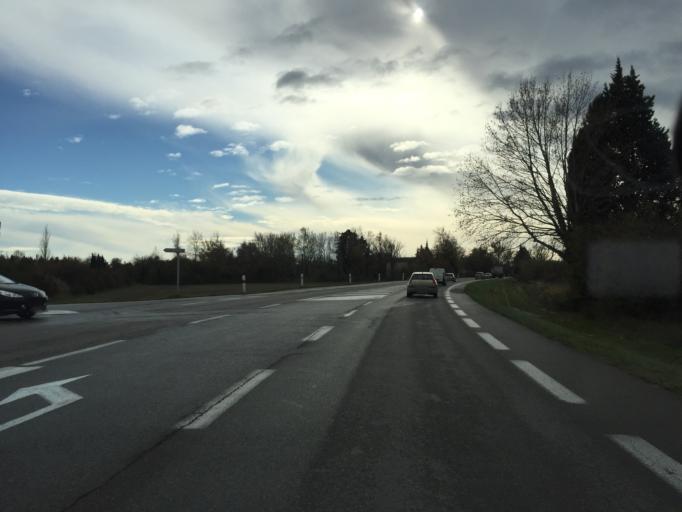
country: FR
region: Provence-Alpes-Cote d'Azur
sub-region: Departement du Vaucluse
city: L'Isle-sur-la-Sorgue
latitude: 43.9292
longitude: 5.0307
